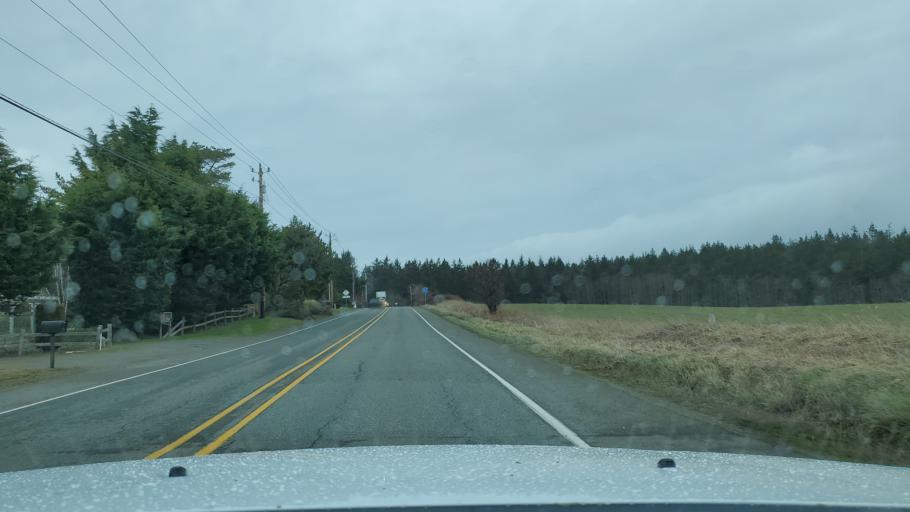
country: US
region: Washington
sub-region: Island County
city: Coupeville
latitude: 48.2835
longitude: -122.7277
